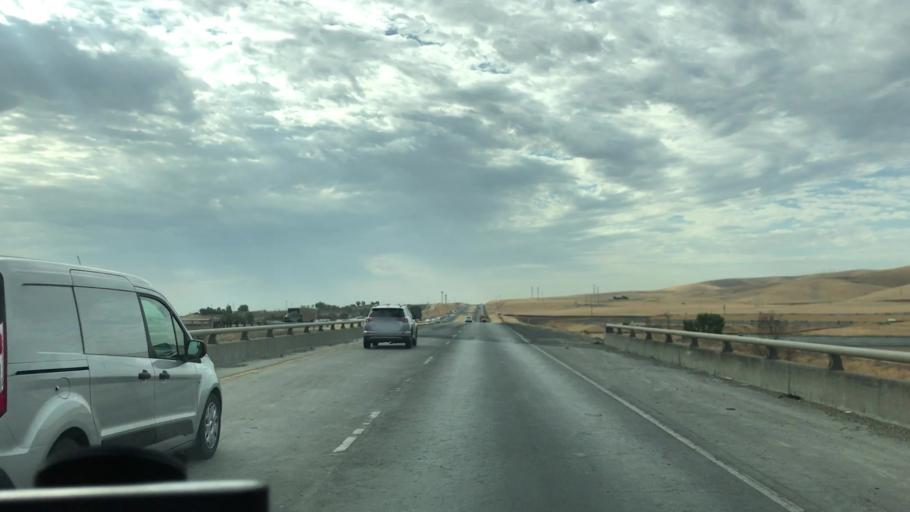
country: US
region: California
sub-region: San Joaquin County
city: Mountain House
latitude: 37.7129
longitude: -121.5248
